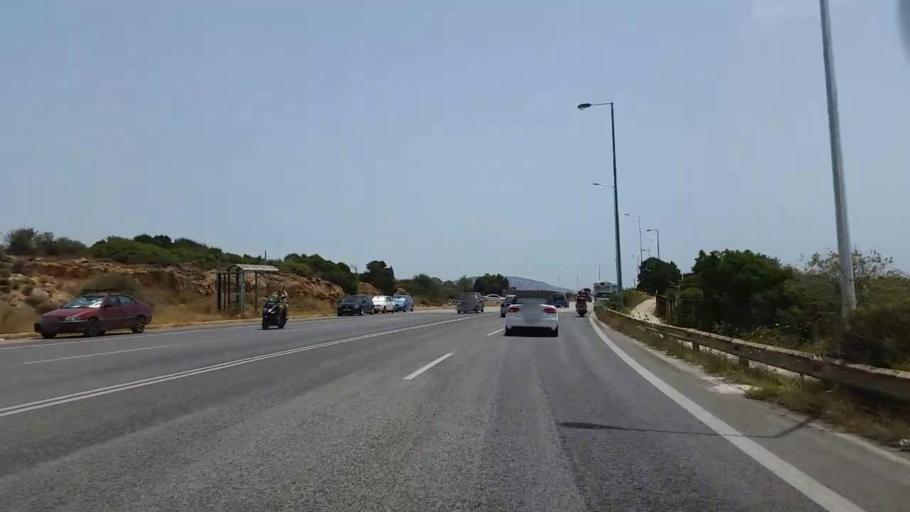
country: GR
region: Attica
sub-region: Nomarchia Anatolikis Attikis
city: Saronida
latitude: 37.7610
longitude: 23.9028
